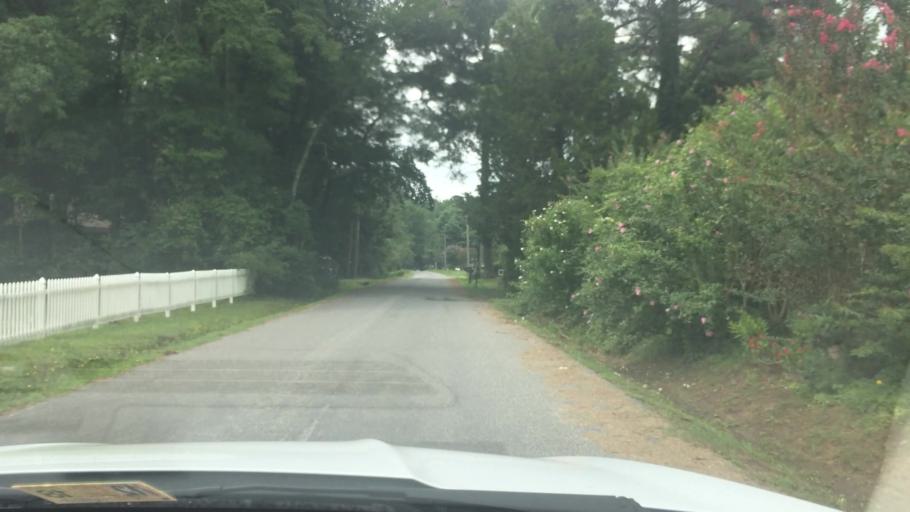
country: US
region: Virginia
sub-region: York County
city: Yorktown
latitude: 37.2320
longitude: -76.5461
